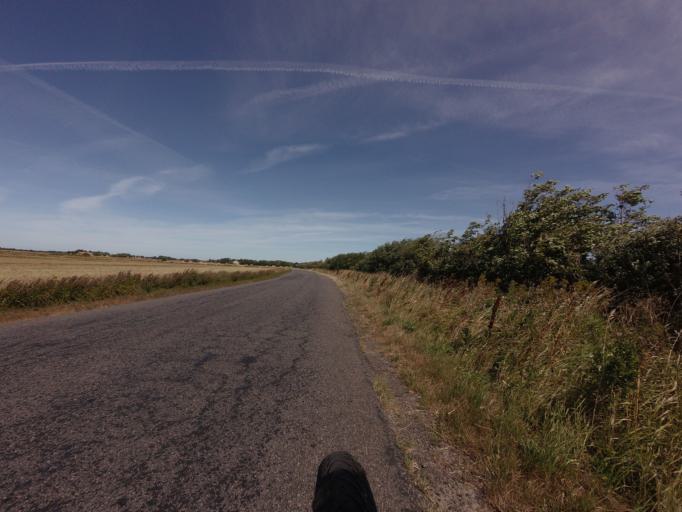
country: DK
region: North Denmark
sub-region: Bronderslev Kommune
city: Bronderslev
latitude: 57.3176
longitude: 9.8150
